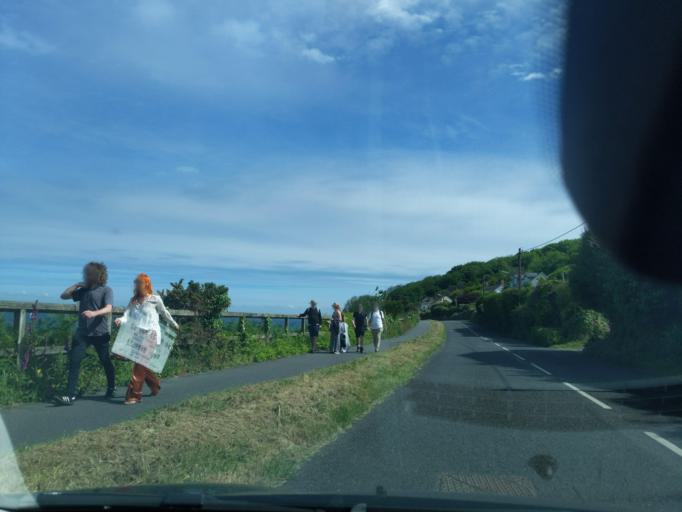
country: GB
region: England
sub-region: Cornwall
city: Penzance
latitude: 50.0929
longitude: -5.5385
